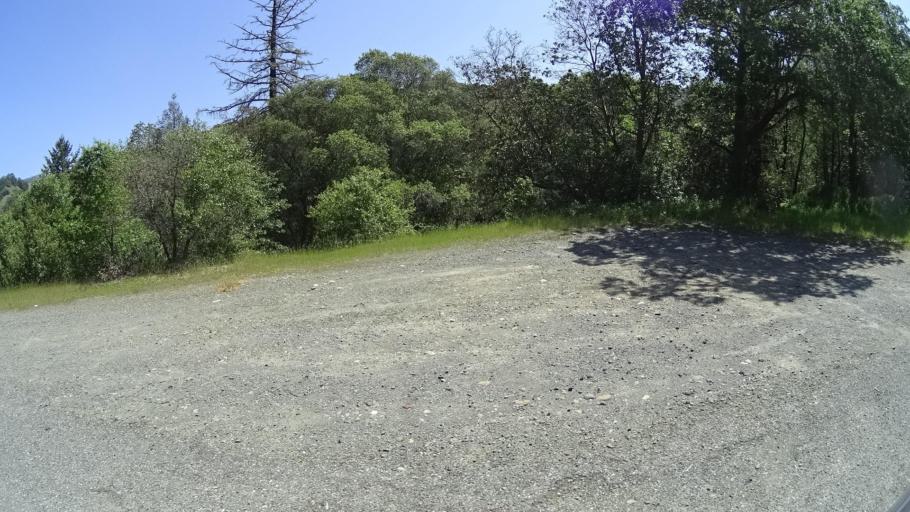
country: US
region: California
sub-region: Humboldt County
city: Redway
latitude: 40.1647
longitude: -123.6032
